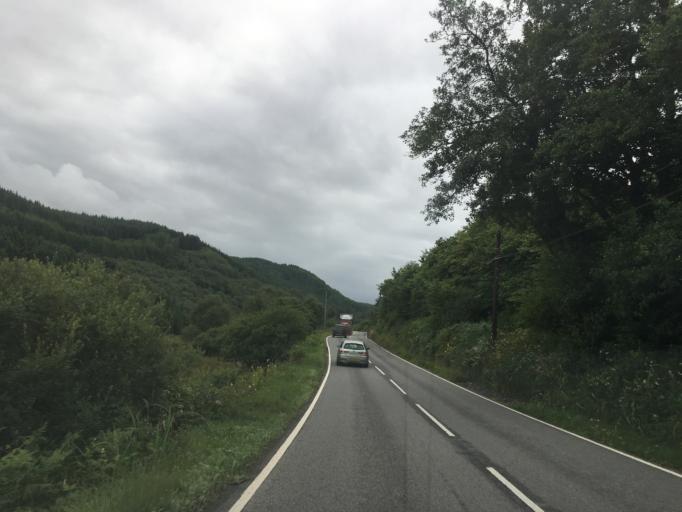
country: GB
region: Scotland
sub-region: Argyll and Bute
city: Oban
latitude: 56.2981
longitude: -5.4639
